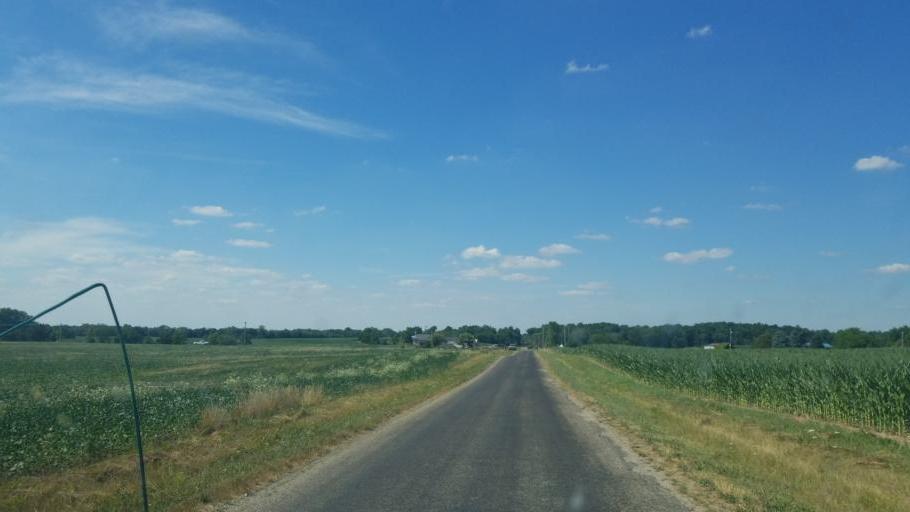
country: US
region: Ohio
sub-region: Williams County
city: Edgerton
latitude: 41.3799
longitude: -84.7863
